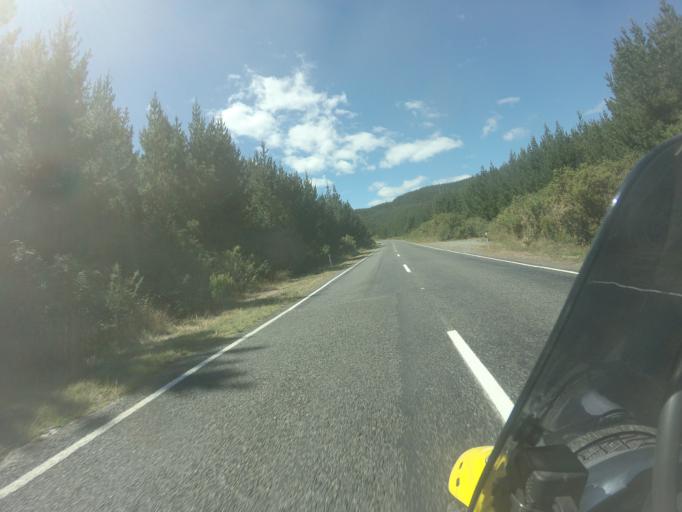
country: NZ
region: Bay of Plenty
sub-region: Whakatane District
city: Murupara
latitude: -38.2849
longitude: 176.8128
